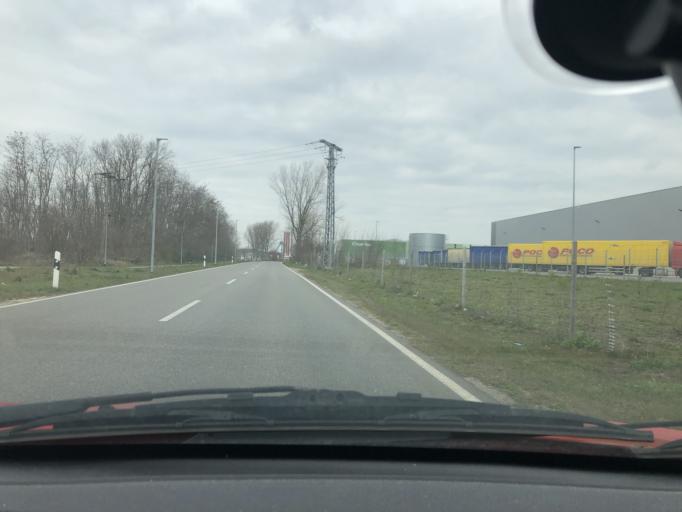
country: DE
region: North Rhine-Westphalia
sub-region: Regierungsbezirk Dusseldorf
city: Kamp-Lintfort
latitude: 51.4829
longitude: 6.5536
